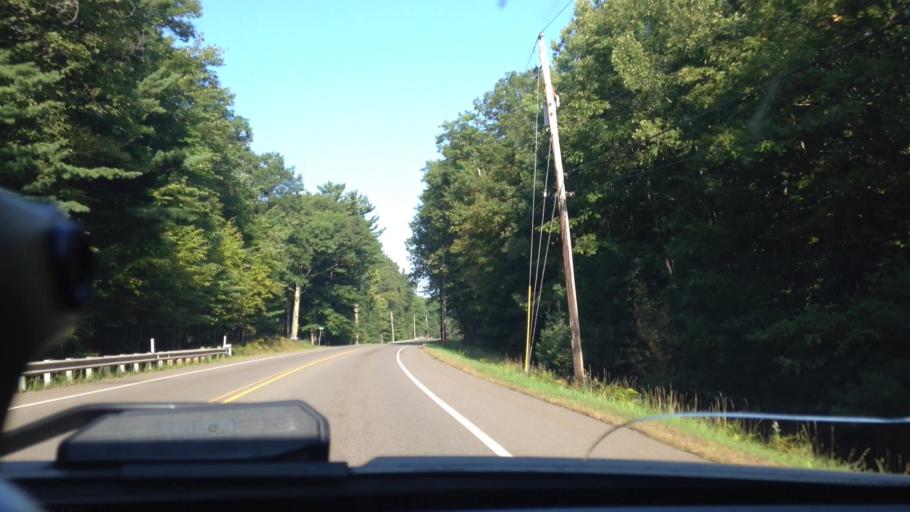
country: US
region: Michigan
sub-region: Dickinson County
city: Quinnesec
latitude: 45.8325
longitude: -88.0047
